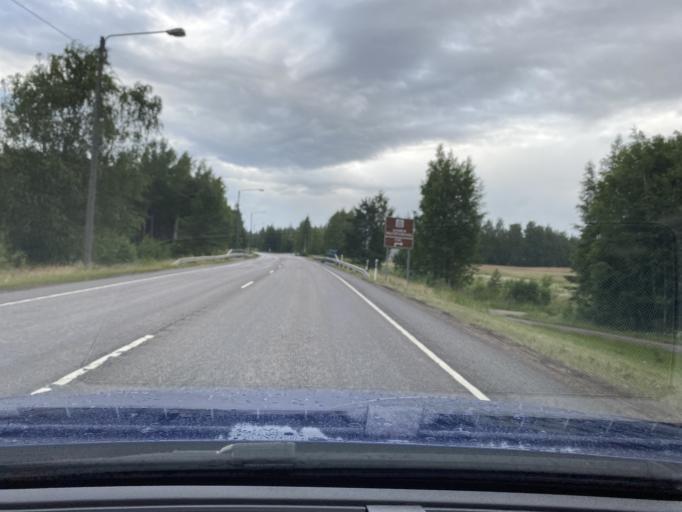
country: FI
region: Uusimaa
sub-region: Helsinki
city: Hyvinge
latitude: 60.6155
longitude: 24.8114
